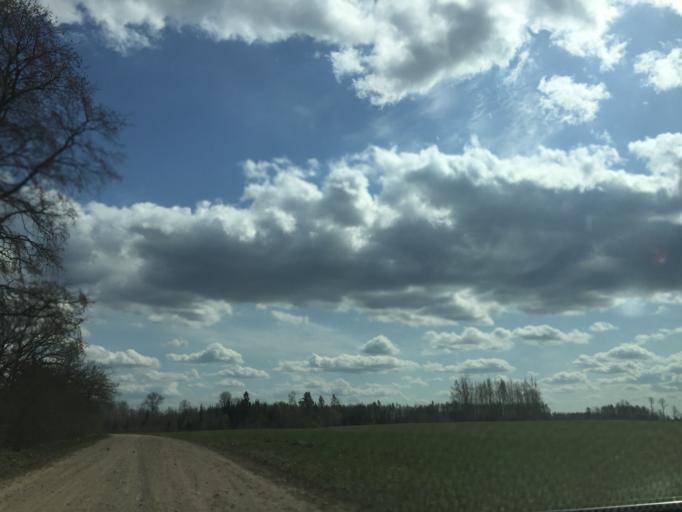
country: LV
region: Skriveri
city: Skriveri
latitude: 56.7599
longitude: 25.1399
